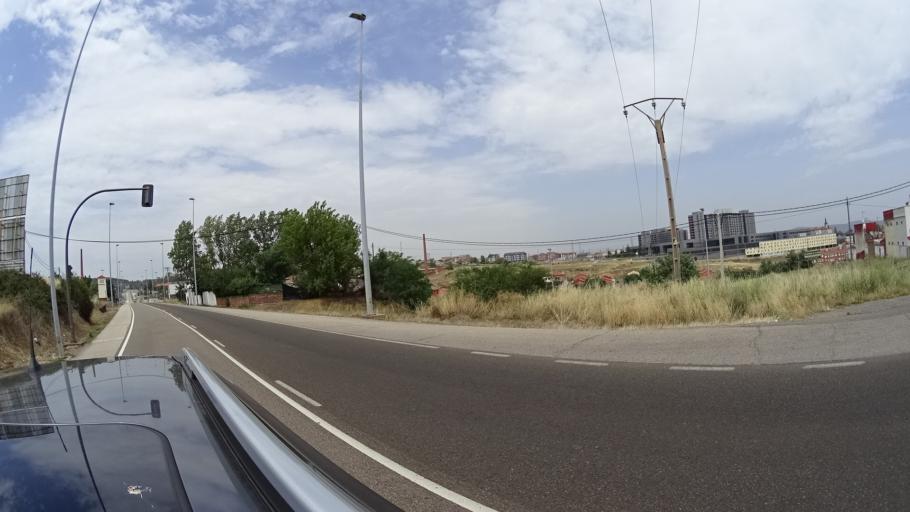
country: ES
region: Castille and Leon
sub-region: Provincia de Leon
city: Leon
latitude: 42.6155
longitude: -5.5786
